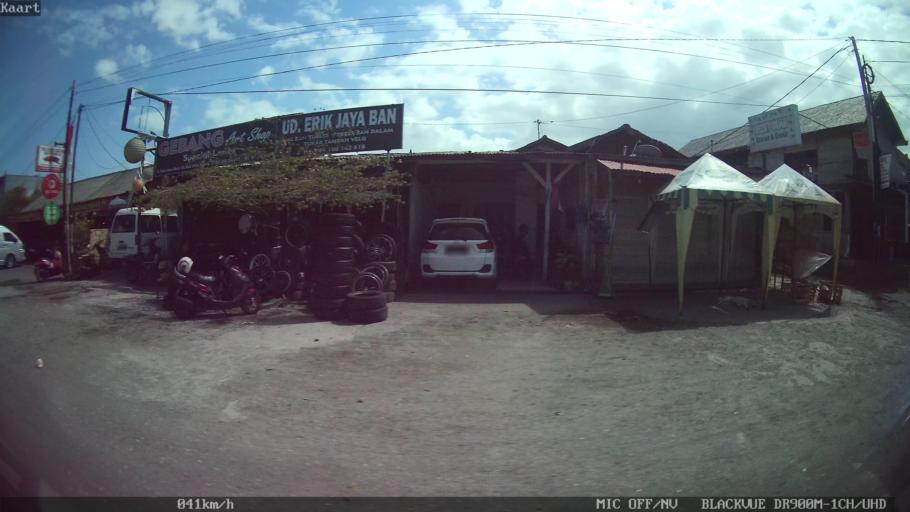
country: ID
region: Bali
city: Denpasar
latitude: -8.6738
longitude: 115.1786
